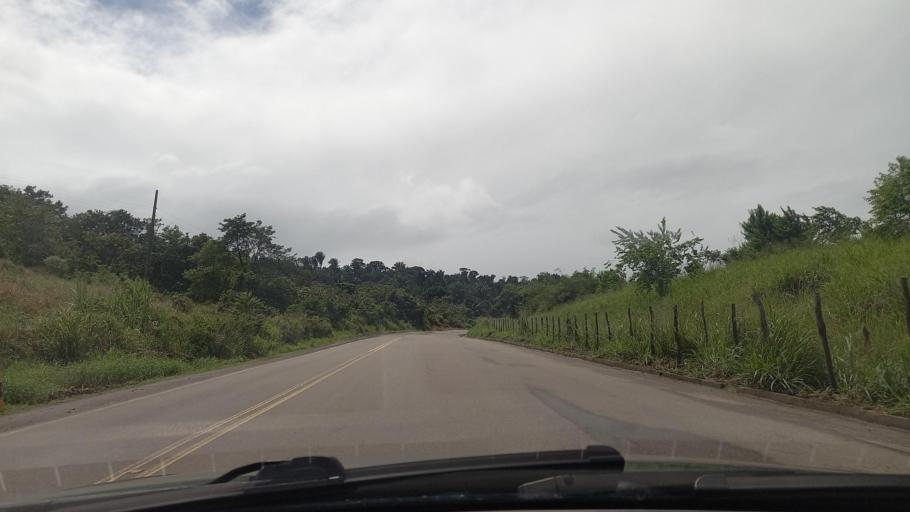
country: BR
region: Alagoas
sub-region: Sao Miguel Dos Campos
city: Sao Miguel dos Campos
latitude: -9.8108
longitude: -36.2216
